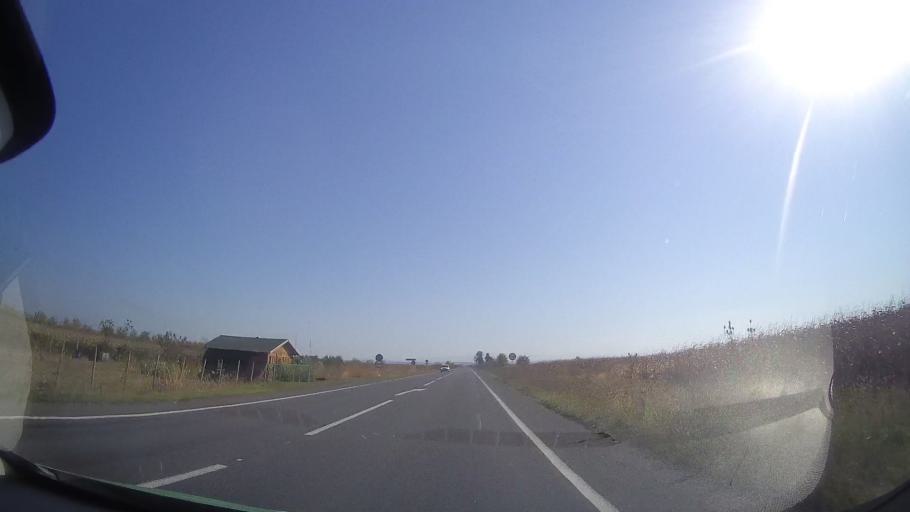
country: RO
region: Timis
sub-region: Comuna Belint
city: Belint
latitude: 45.7468
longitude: 21.7905
